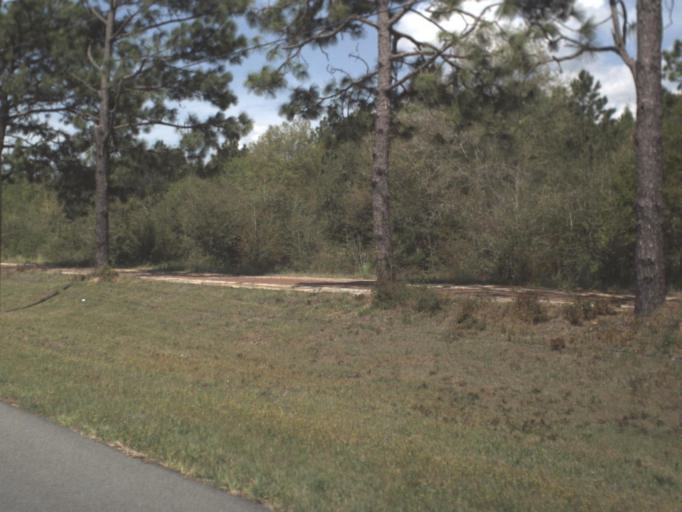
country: US
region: Florida
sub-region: Santa Rosa County
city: East Milton
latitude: 30.6405
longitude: -86.9479
